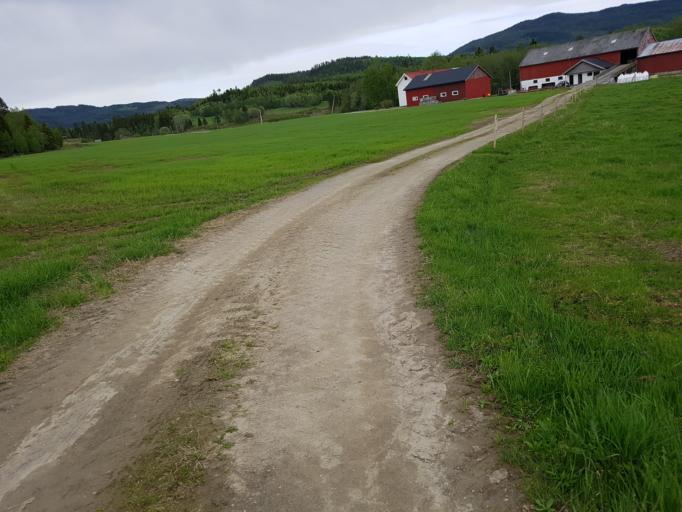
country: NO
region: Nord-Trondelag
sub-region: Levanger
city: Skogn
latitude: 63.6309
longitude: 11.2574
